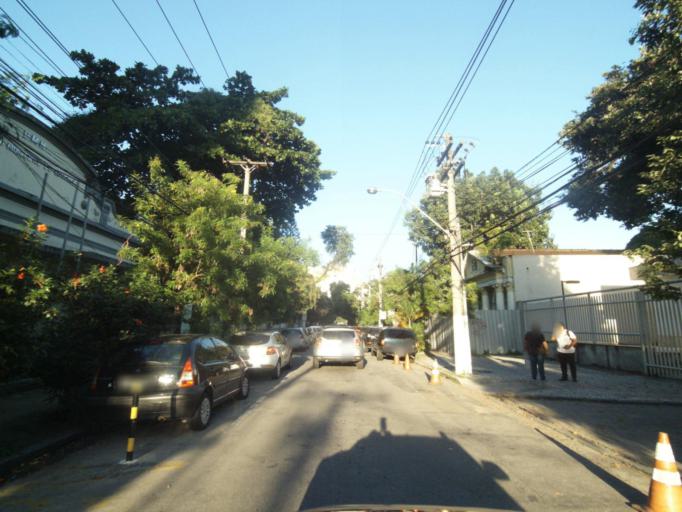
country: BR
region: Rio de Janeiro
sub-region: Niteroi
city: Niteroi
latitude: -22.8927
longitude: -43.1177
